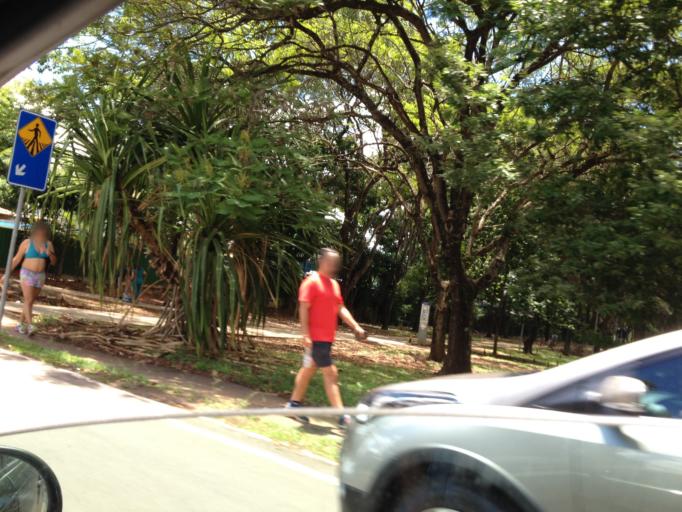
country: BR
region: Federal District
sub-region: Brasilia
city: Brasilia
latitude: -15.8170
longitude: -47.9066
